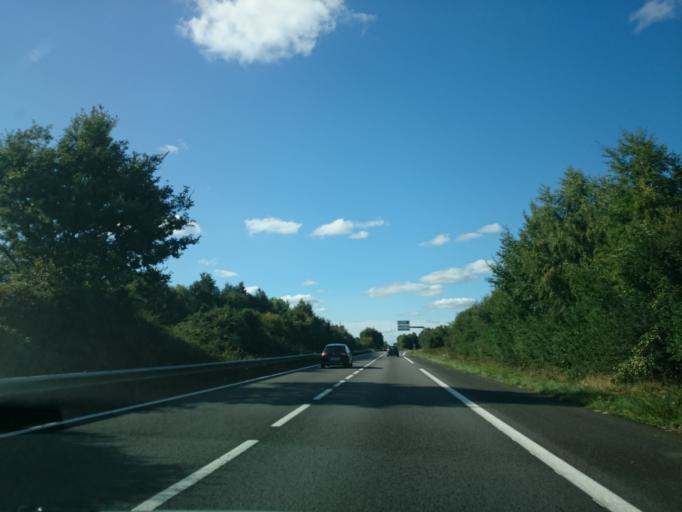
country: FR
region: Pays de la Loire
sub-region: Departement de la Loire-Atlantique
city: Jans
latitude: 47.6215
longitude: -1.6398
